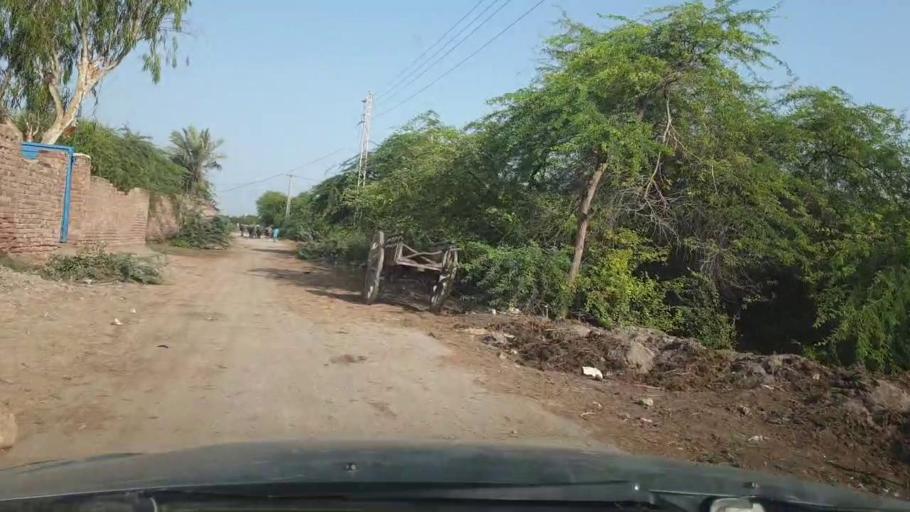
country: PK
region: Sindh
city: Tando Ghulam Ali
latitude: 25.2083
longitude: 68.9360
